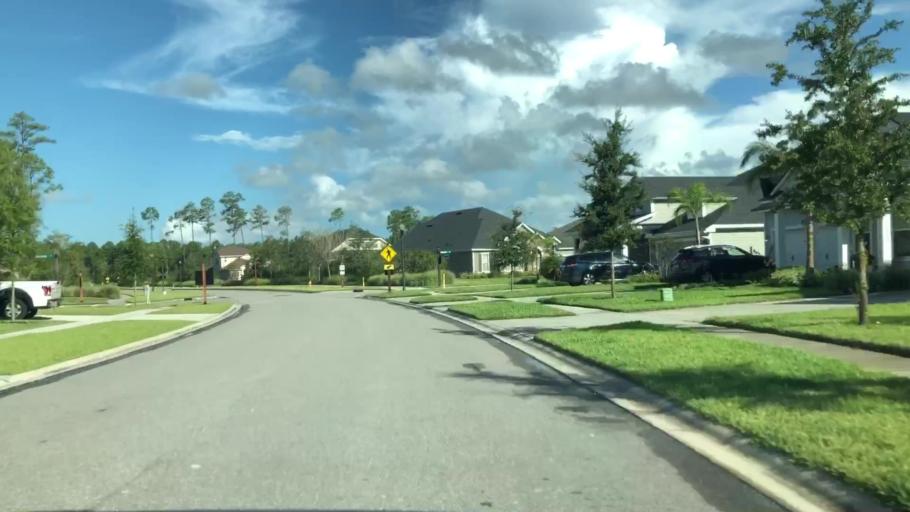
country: US
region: Florida
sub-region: Saint Johns County
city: Palm Valley
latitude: 30.1291
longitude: -81.4086
